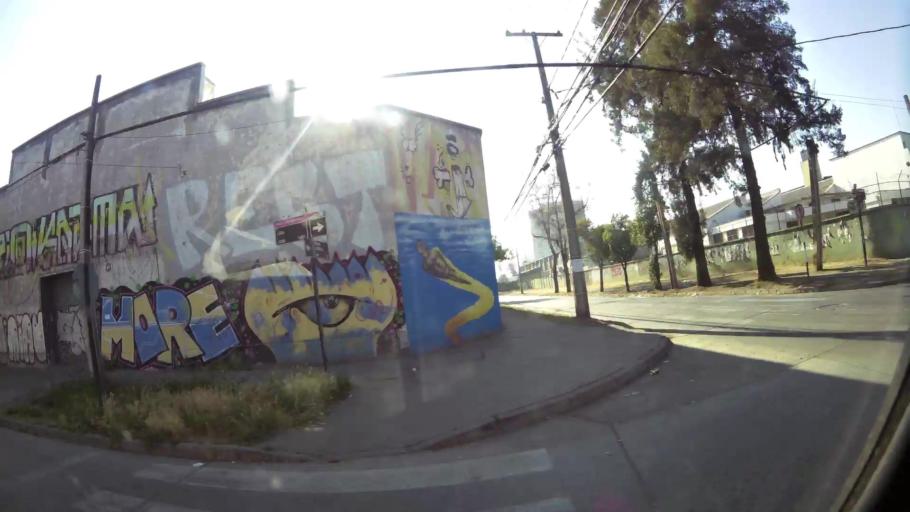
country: CL
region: Santiago Metropolitan
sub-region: Provincia de Santiago
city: Santiago
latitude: -33.4762
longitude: -70.6313
